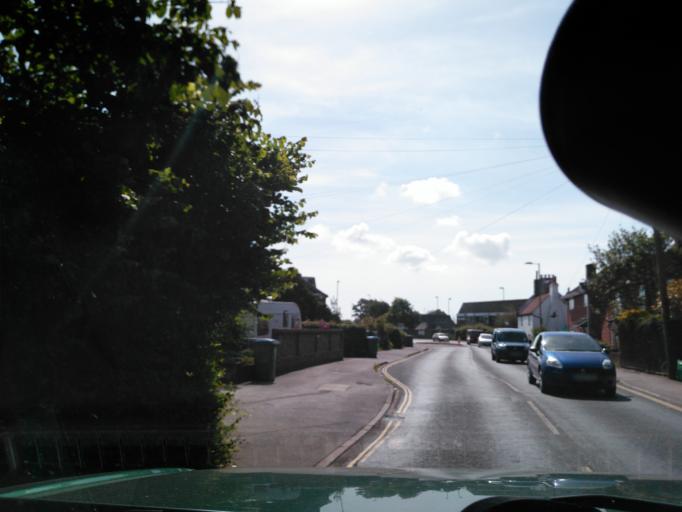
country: GB
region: England
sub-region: Hampshire
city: Lee-on-the-Solent
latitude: 50.8271
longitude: -1.2153
